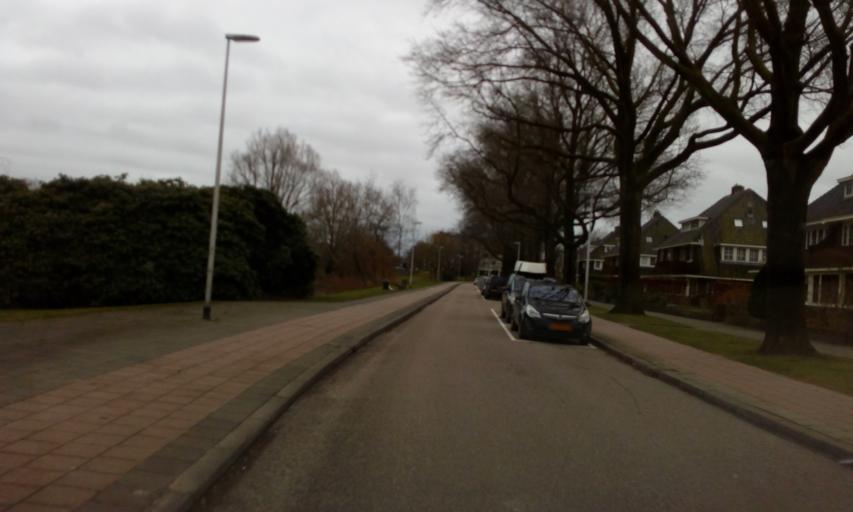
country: NL
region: North Holland
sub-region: Gemeente Bussum
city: Bussum
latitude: 52.2778
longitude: 5.1719
